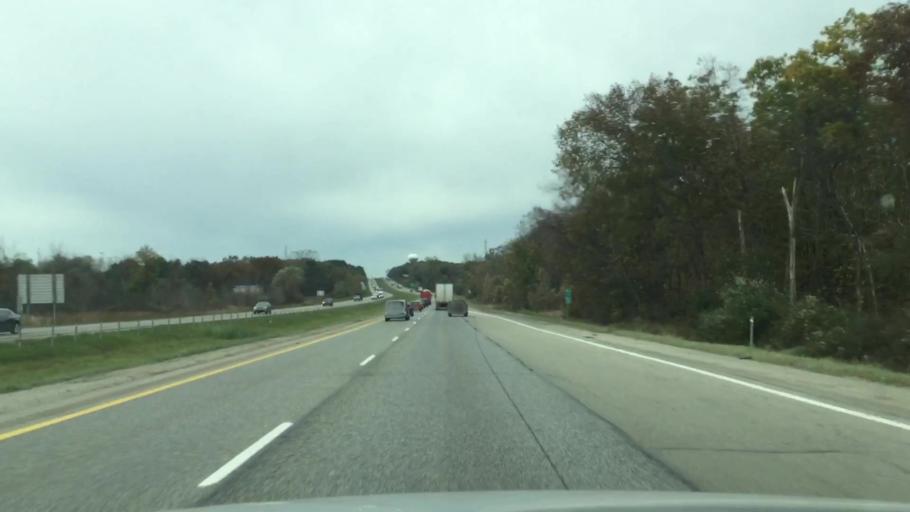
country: US
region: Michigan
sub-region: Washtenaw County
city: Chelsea
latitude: 42.2946
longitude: -84.0351
